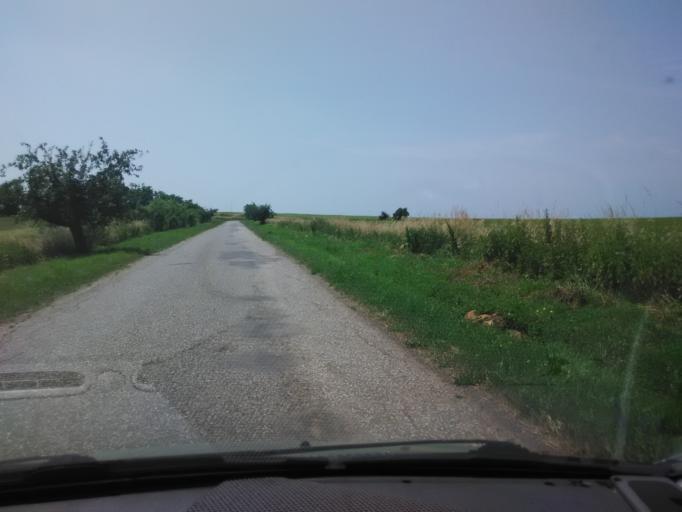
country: SK
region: Nitriansky
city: Levice
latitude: 48.2391
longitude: 18.6405
